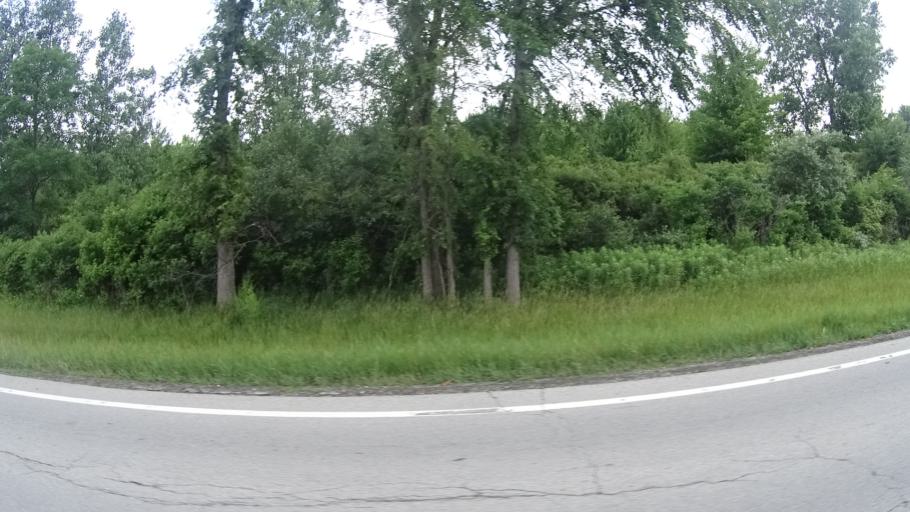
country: US
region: Ohio
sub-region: Huron County
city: Wakeman
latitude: 41.3055
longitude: -82.4821
